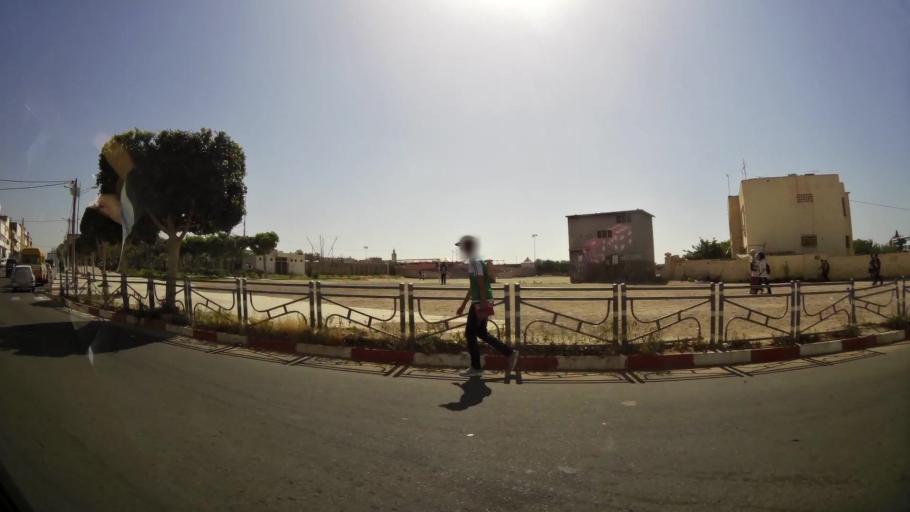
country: MA
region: Souss-Massa-Draa
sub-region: Inezgane-Ait Mellou
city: Inezgane
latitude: 30.3576
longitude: -9.5382
